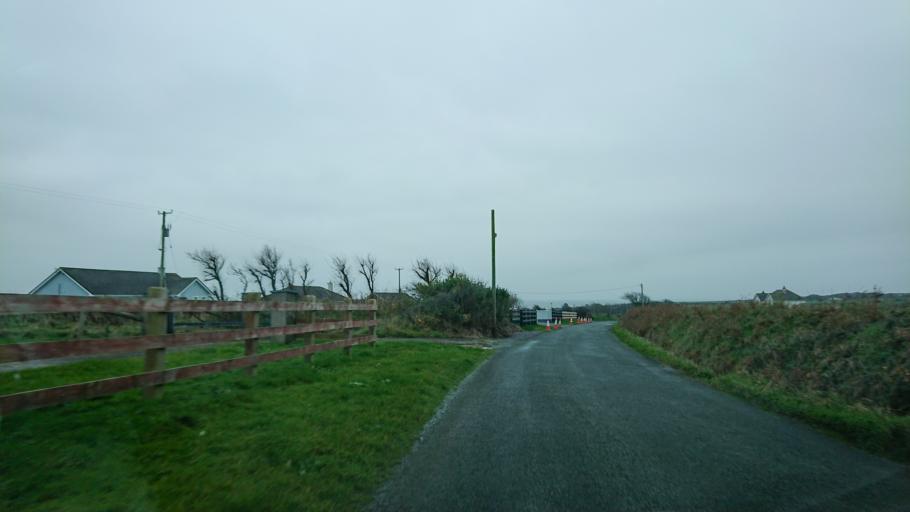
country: IE
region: Munster
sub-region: Waterford
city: Dunmore East
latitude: 52.1531
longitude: -7.0584
